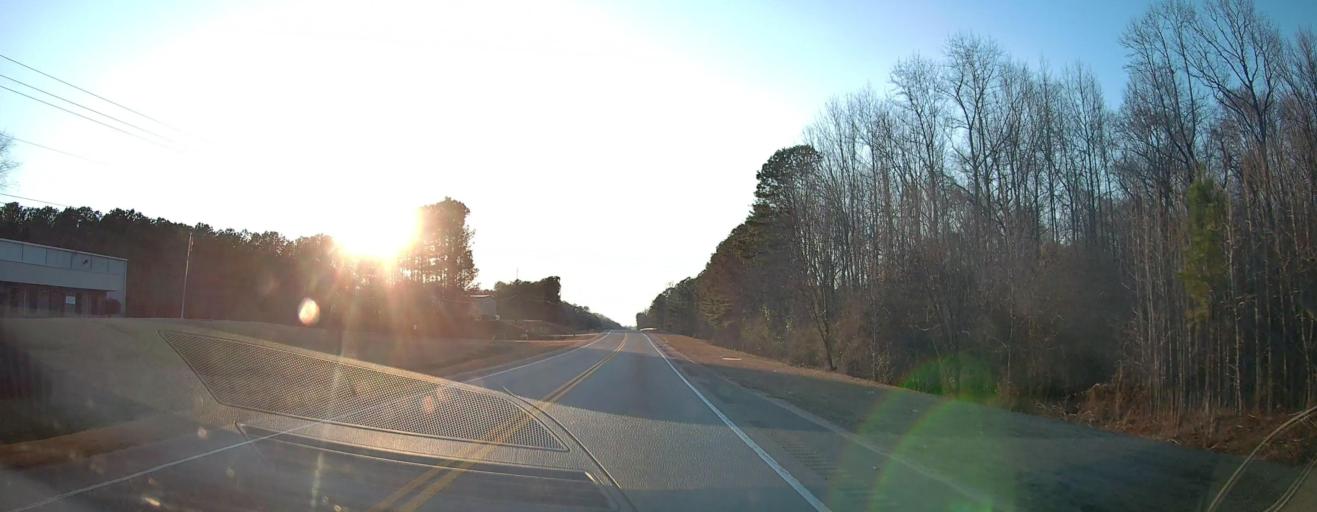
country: US
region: Georgia
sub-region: Troup County
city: La Grange
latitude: 32.9891
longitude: -85.0430
